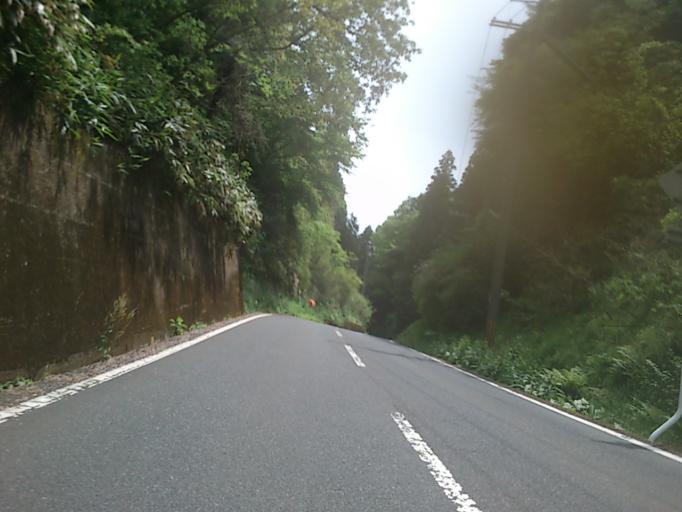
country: JP
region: Kyoto
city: Miyazu
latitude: 35.5873
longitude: 135.1200
